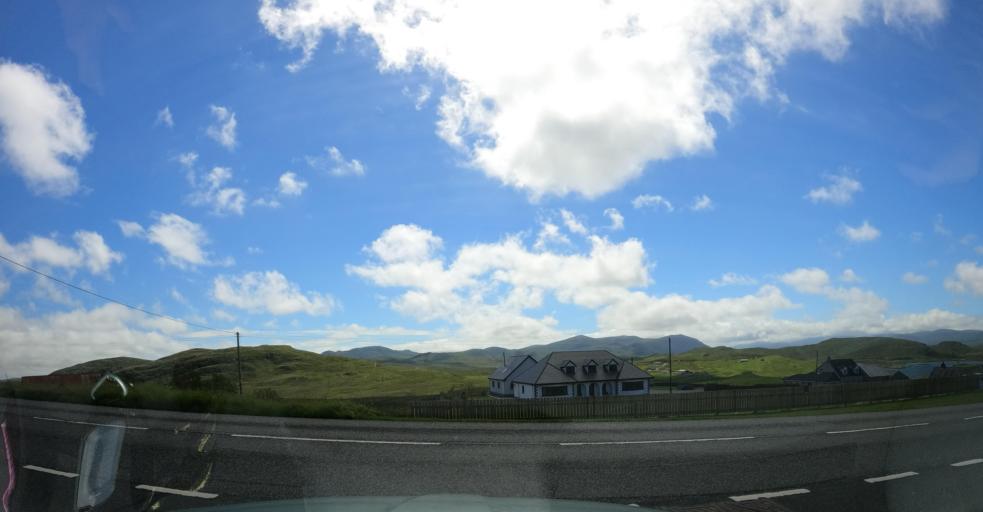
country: GB
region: Scotland
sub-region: Eilean Siar
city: Stornoway
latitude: 58.0914
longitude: -6.6057
